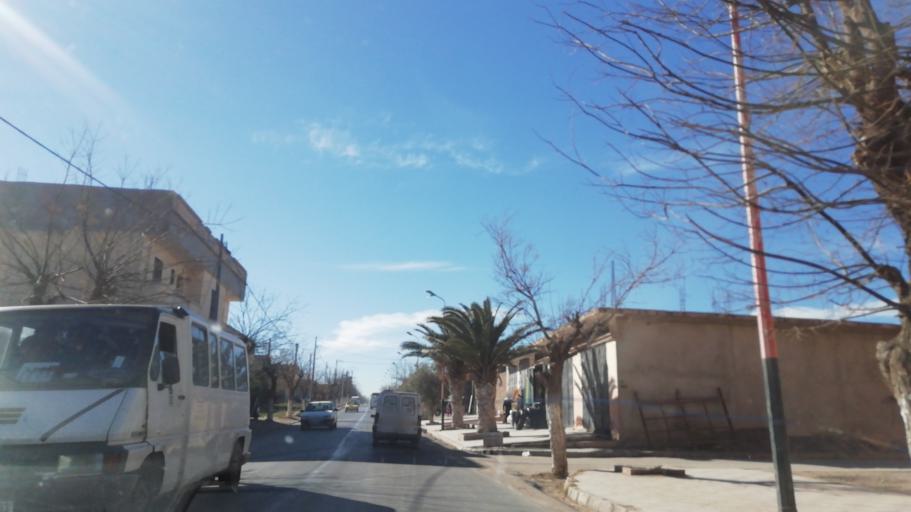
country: DZ
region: Tlemcen
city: Sebdou
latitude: 34.6519
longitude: -1.3184
